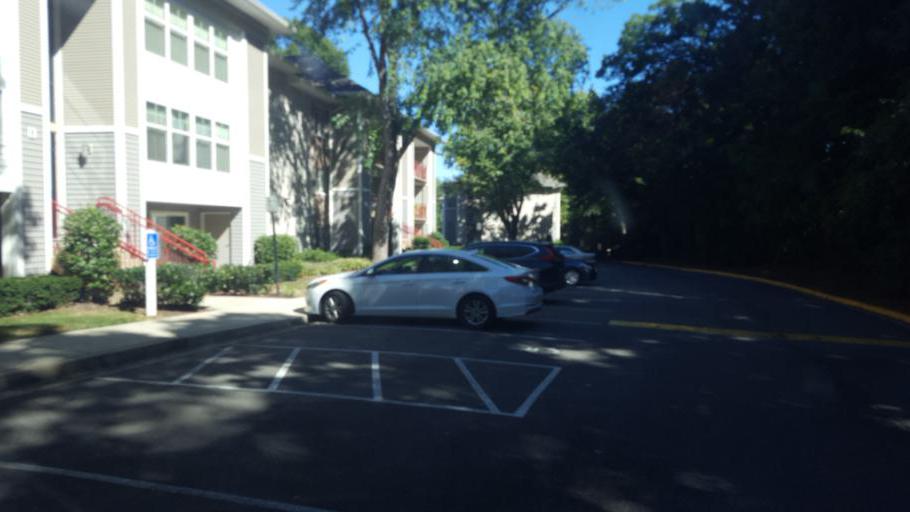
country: US
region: Virginia
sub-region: Fairfax County
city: Baileys Crossroads
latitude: 38.8280
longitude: -77.1076
